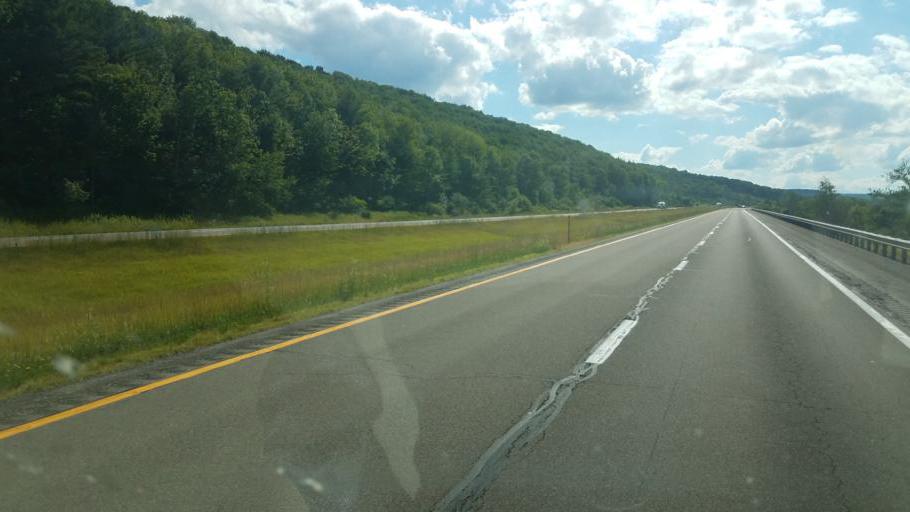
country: US
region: New York
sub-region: Allegany County
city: Alfred
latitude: 42.3170
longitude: -77.7783
